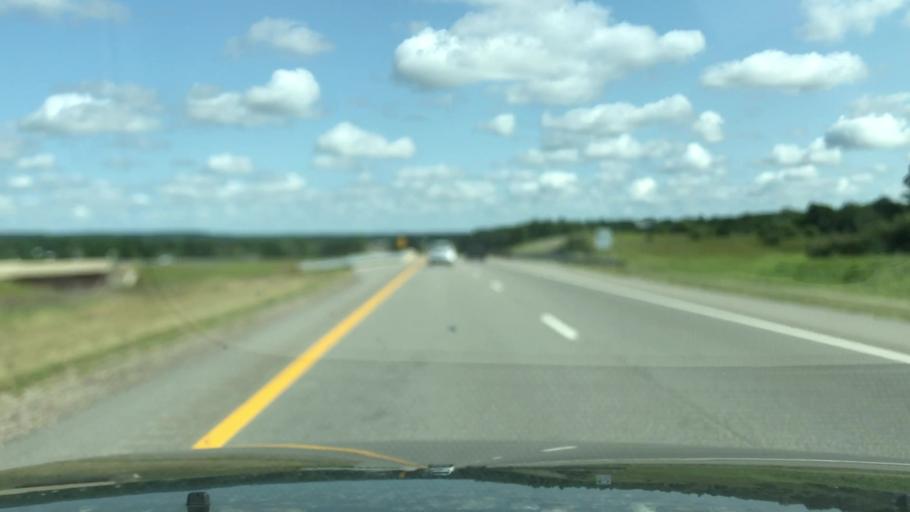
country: US
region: Michigan
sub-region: Mecosta County
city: Big Rapids
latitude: 43.5825
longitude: -85.4891
